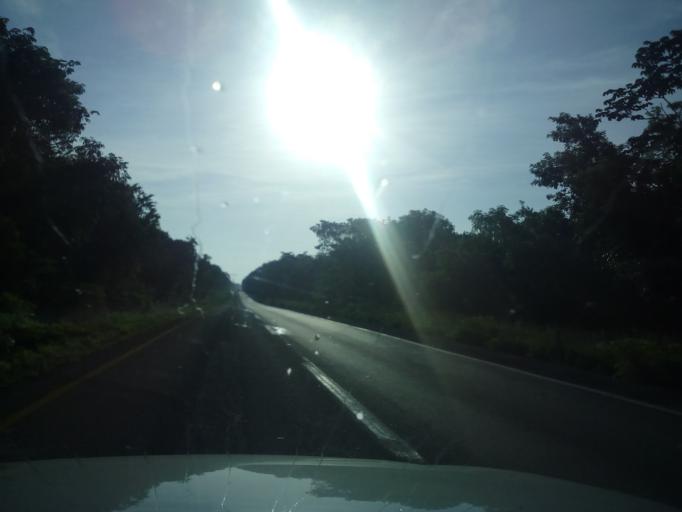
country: MX
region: Yucatan
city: Piste
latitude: 20.7364
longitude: -88.6179
